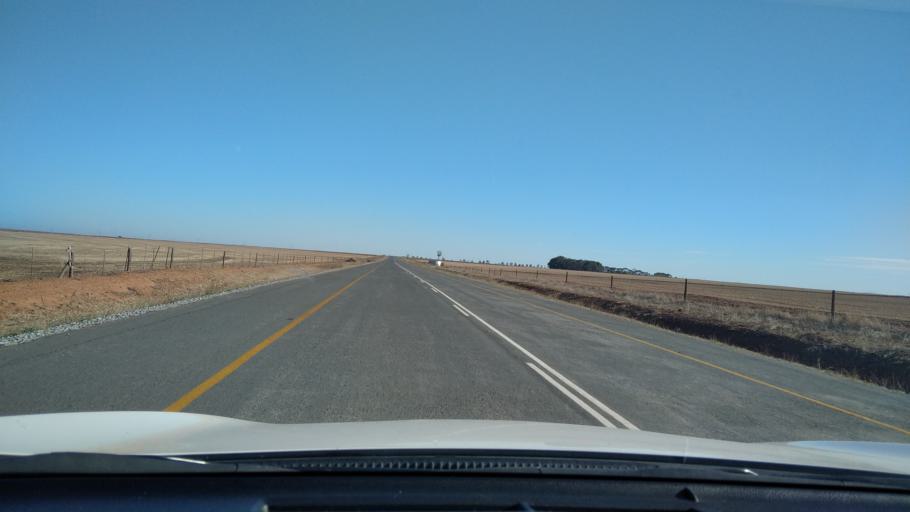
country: ZA
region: Western Cape
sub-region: West Coast District Municipality
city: Malmesbury
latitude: -33.3350
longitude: 18.6332
